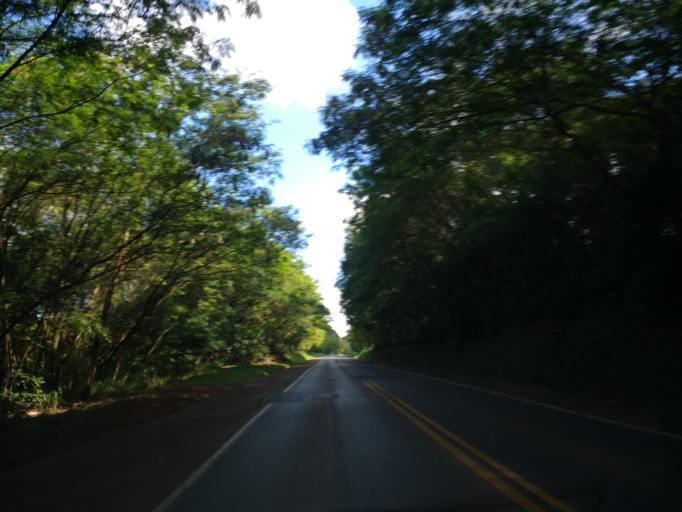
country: BR
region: Parana
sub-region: Umuarama
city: Umuarama
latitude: -23.8829
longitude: -53.3980
